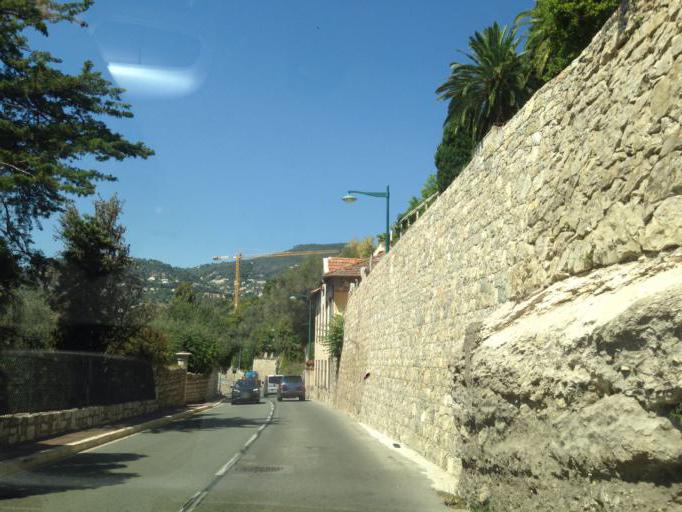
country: FR
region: Provence-Alpes-Cote d'Azur
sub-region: Departement des Alpes-Maritimes
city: Saint-Jean-Cap-Ferrat
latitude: 43.6950
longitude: 7.3282
